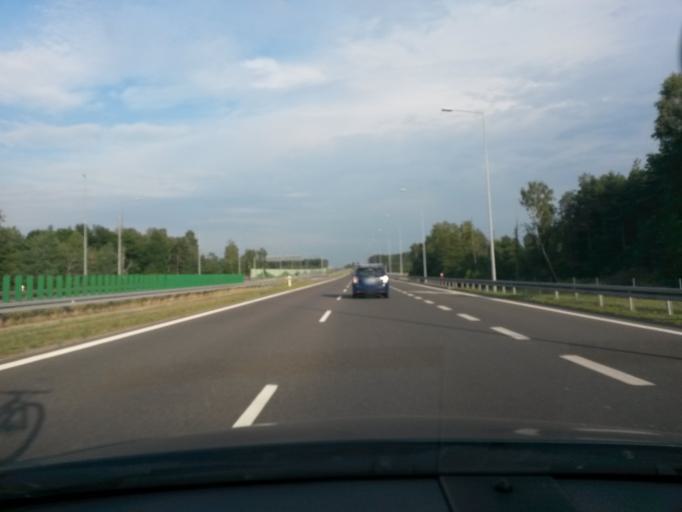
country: PL
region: Lodz Voivodeship
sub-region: Powiat zgierski
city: Zgierz
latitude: 51.9087
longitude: 19.4417
